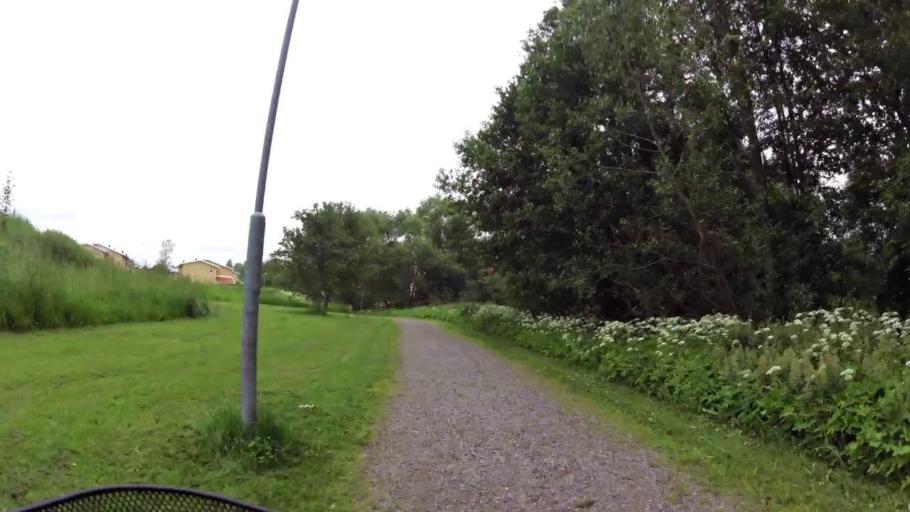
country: SE
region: OEstergoetland
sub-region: Linkopings Kommun
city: Linkoping
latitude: 58.3716
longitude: 15.6629
